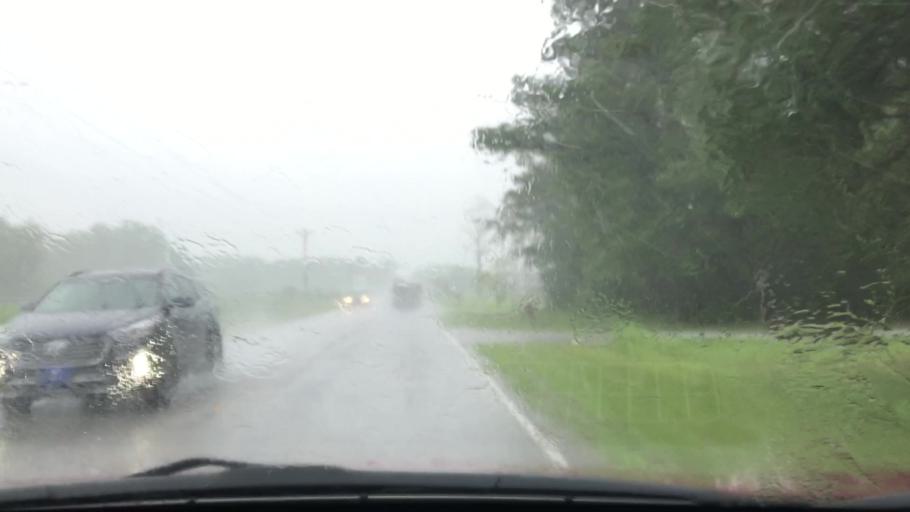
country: US
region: South Carolina
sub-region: Horry County
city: Red Hill
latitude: 33.8949
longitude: -78.9397
